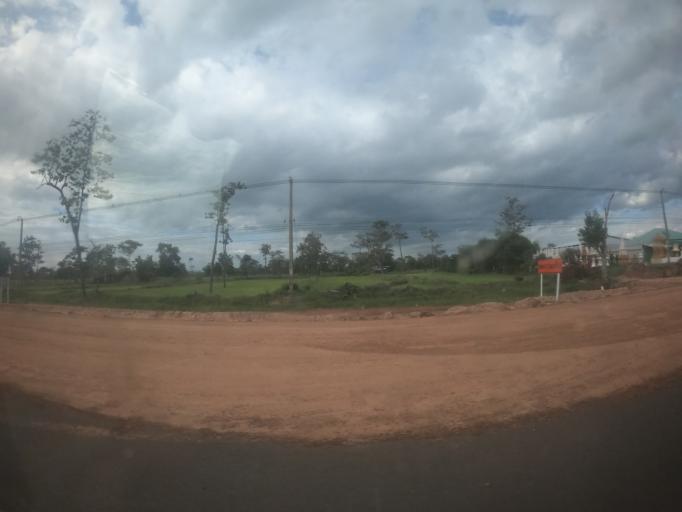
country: TH
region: Surin
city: Kap Choeng
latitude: 14.5163
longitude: 103.5464
